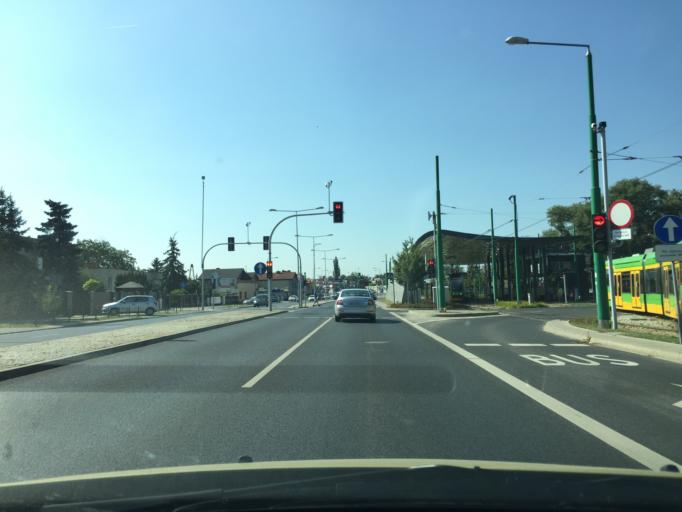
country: PL
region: Greater Poland Voivodeship
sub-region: Powiat poznanski
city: Plewiska
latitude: 52.3837
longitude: 16.8356
